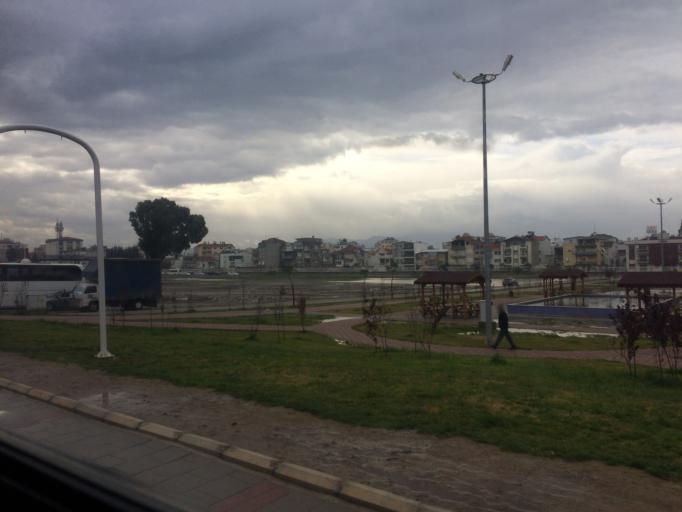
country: TR
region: Izmir
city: Karsiyaka
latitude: 38.4968
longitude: 27.0589
